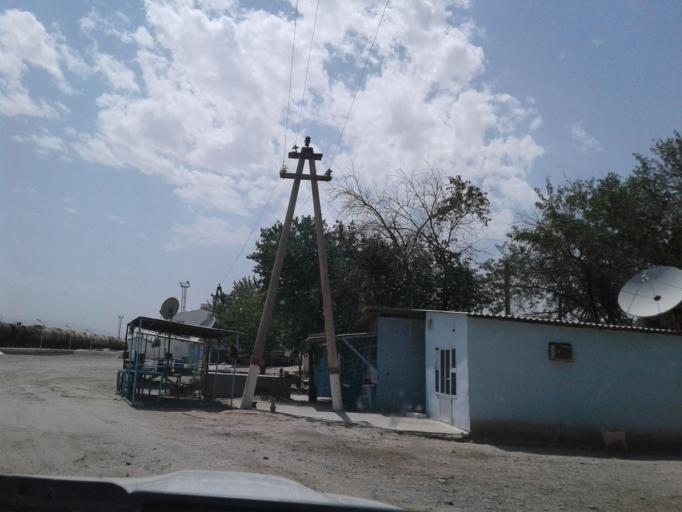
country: IR
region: Razavi Khorasan
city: Kalat-e Naderi
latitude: 37.2007
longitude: 60.0314
